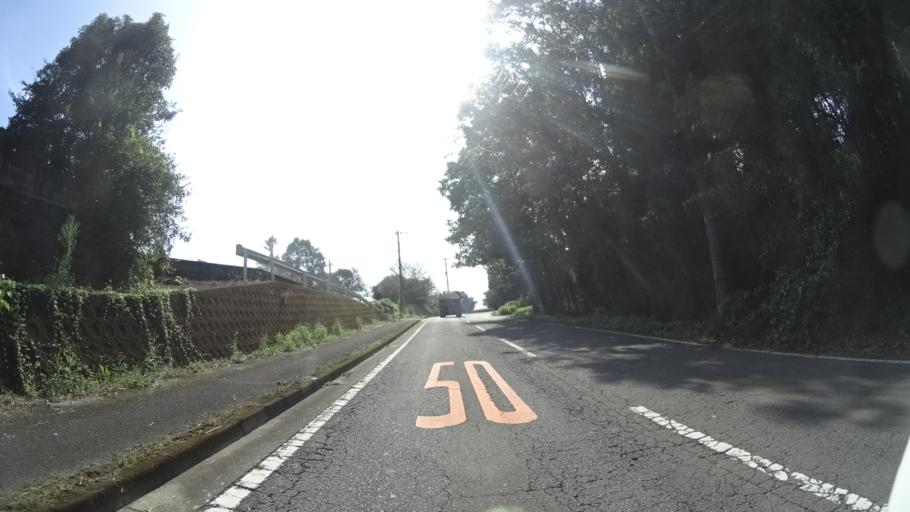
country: JP
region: Miyazaki
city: Kobayashi
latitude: 32.0364
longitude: 130.8213
